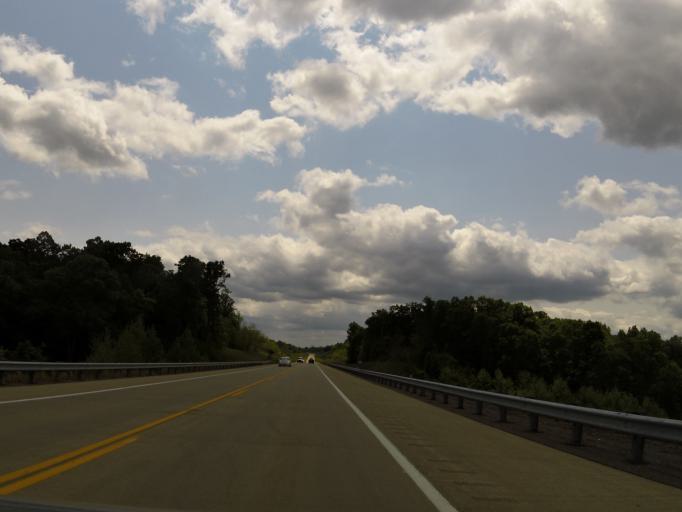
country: US
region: Ohio
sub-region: Athens County
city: Athens
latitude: 39.2519
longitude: -82.0806
